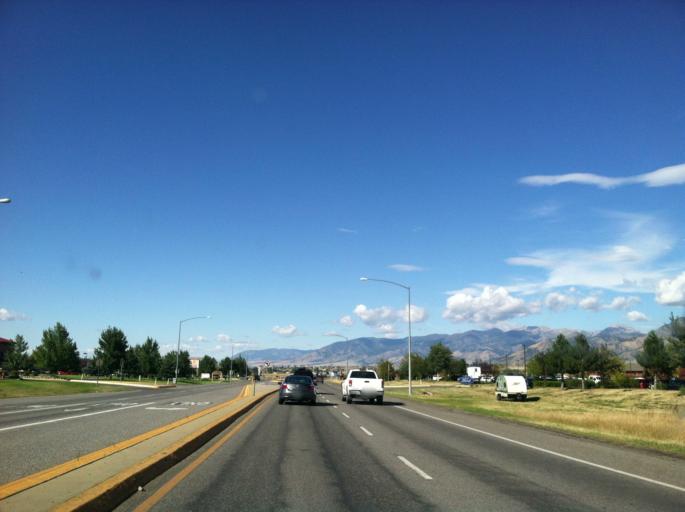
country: US
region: Montana
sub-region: Gallatin County
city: Bozeman
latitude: 45.7084
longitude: -111.0655
